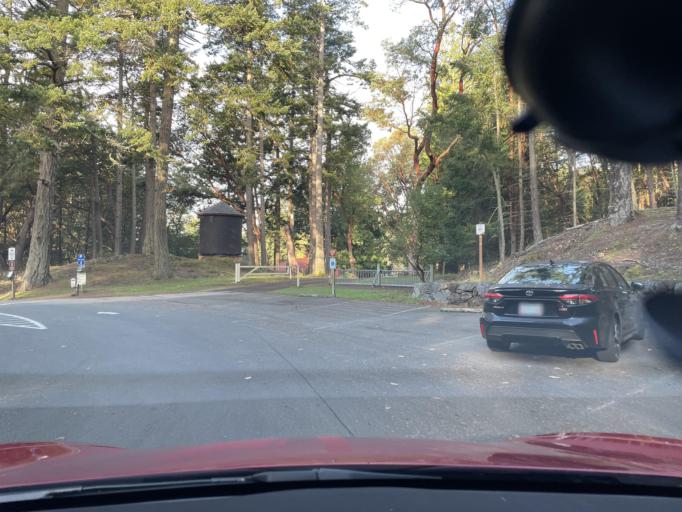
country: US
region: Washington
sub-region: San Juan County
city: Friday Harbor
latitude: 48.5155
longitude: -123.1491
